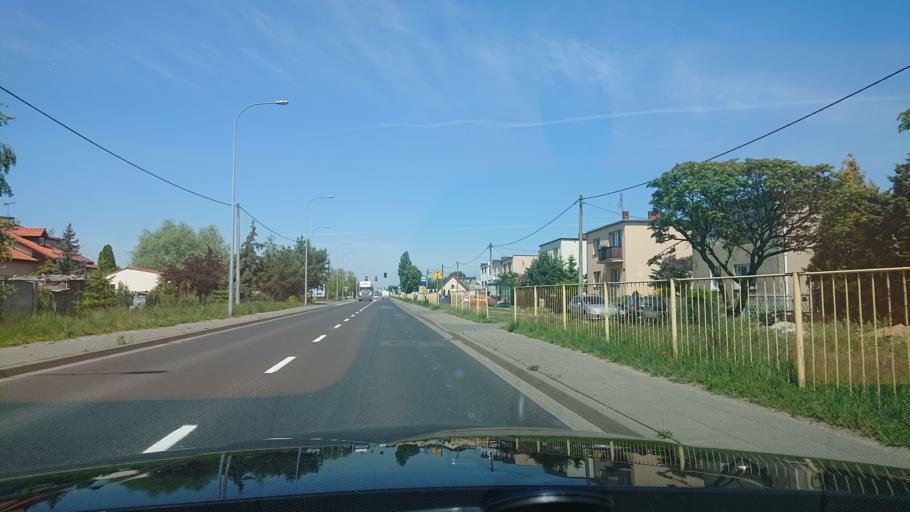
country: PL
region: Greater Poland Voivodeship
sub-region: Powiat gnieznienski
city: Gniezno
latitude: 52.5102
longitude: 17.6184
